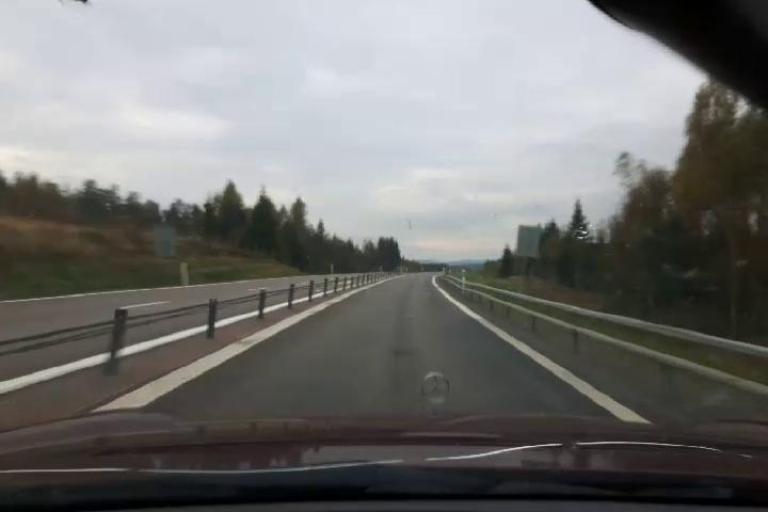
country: SE
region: Vaesternorrland
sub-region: Haernoesands Kommun
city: Haernoesand
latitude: 62.7174
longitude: 17.9119
